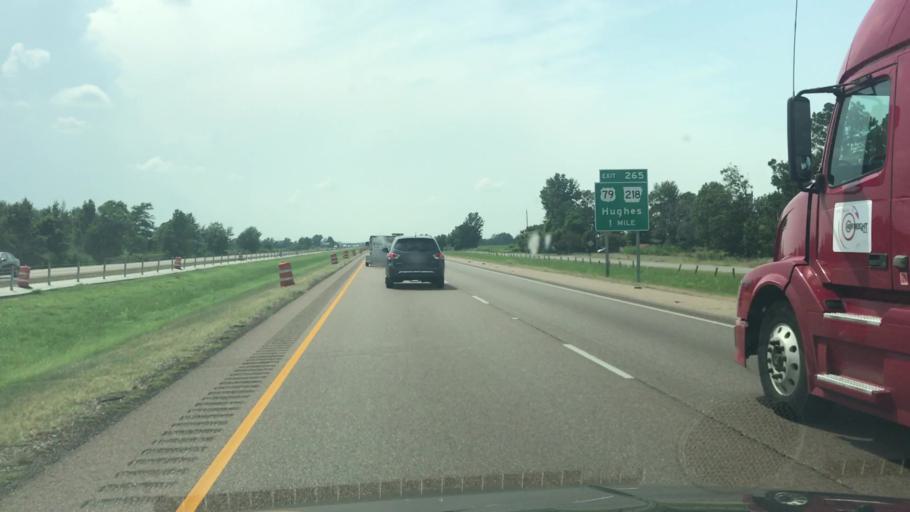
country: US
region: Arkansas
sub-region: Crittenden County
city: Earle
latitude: 35.1507
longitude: -90.3787
